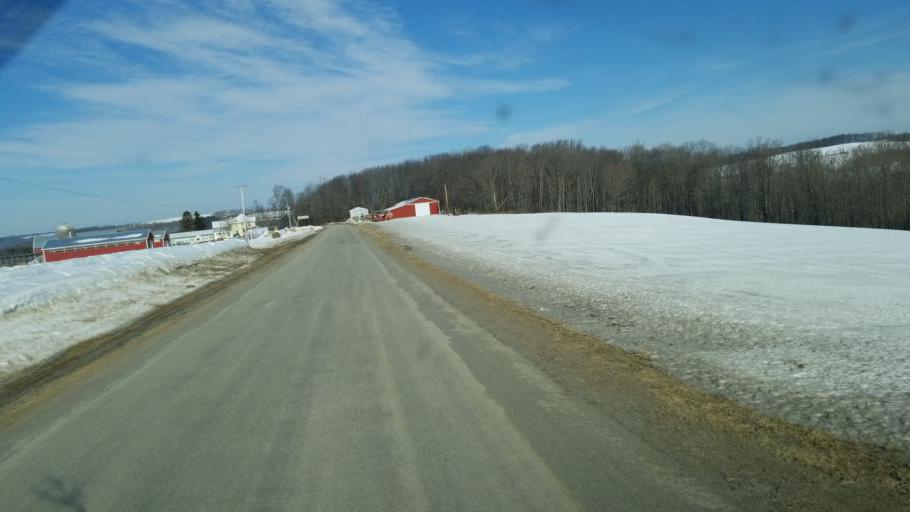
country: US
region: New York
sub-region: Allegany County
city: Andover
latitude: 42.1407
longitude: -77.7592
